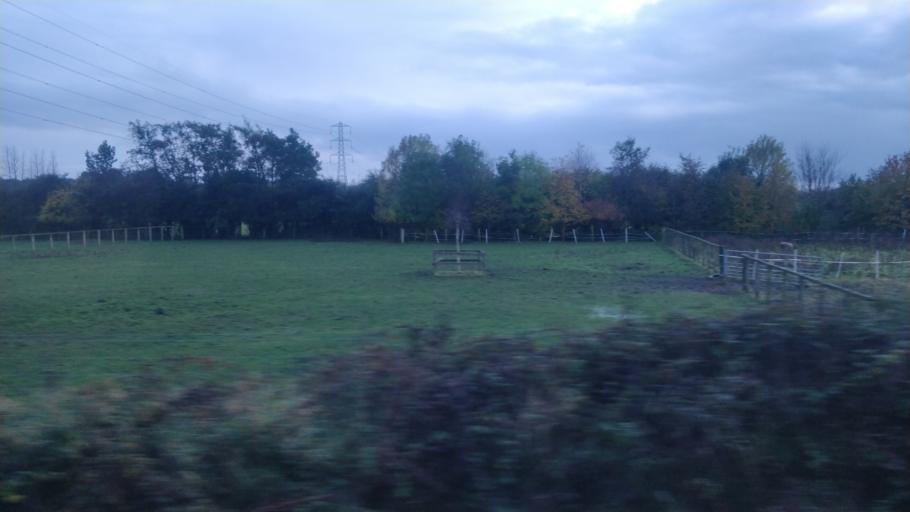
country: GB
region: England
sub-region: Lancashire
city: Parbold
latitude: 53.5965
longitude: -2.7983
